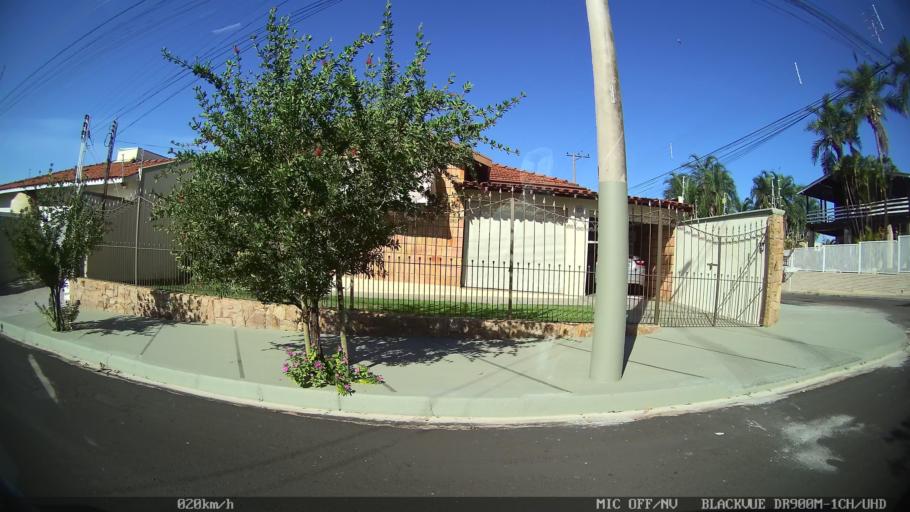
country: BR
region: Sao Paulo
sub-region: Olimpia
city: Olimpia
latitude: -20.7306
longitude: -48.9164
